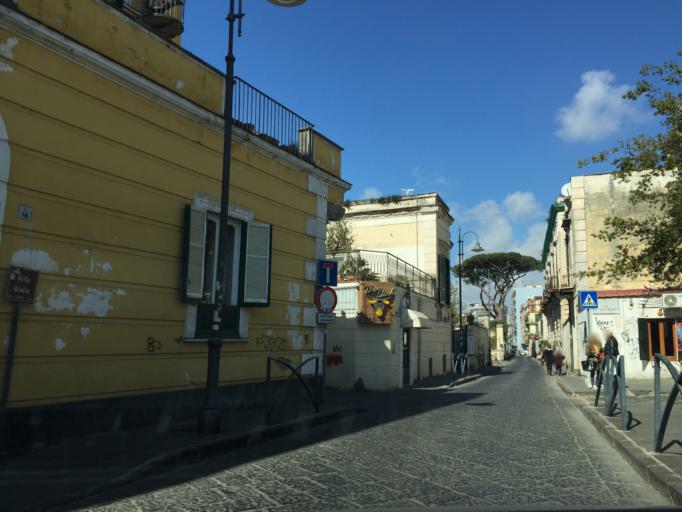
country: IT
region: Campania
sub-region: Provincia di Napoli
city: San Giorgio a Cremano
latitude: 40.8284
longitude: 14.3393
